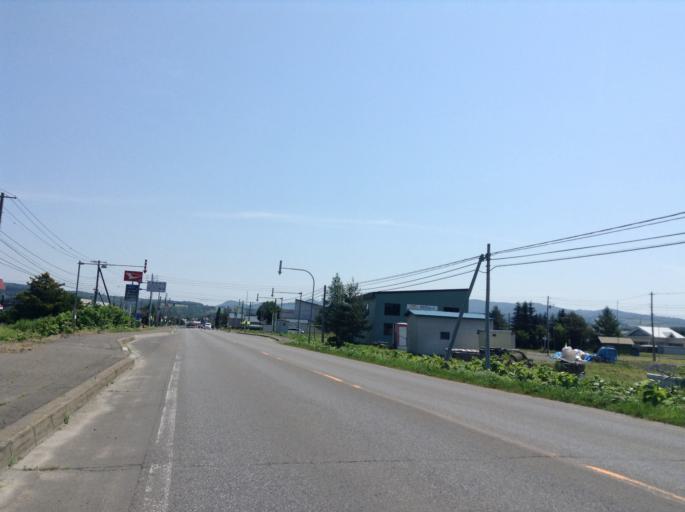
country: JP
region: Hokkaido
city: Nayoro
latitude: 44.3049
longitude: 142.6238
